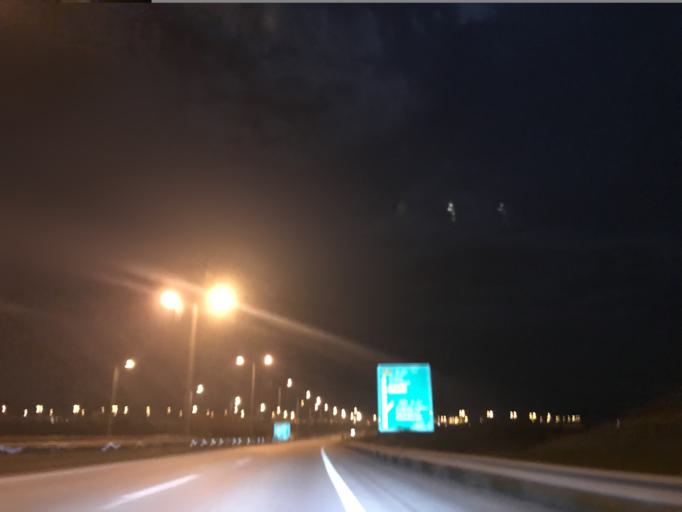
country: TR
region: Hatay
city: Mahmutlar
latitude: 36.9649
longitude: 36.1049
